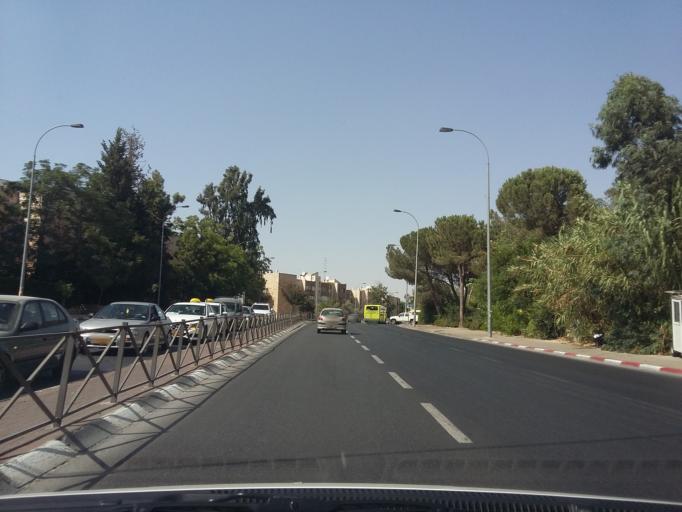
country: IL
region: Jerusalem
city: West Jerusalem
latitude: 31.7973
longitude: 35.2225
